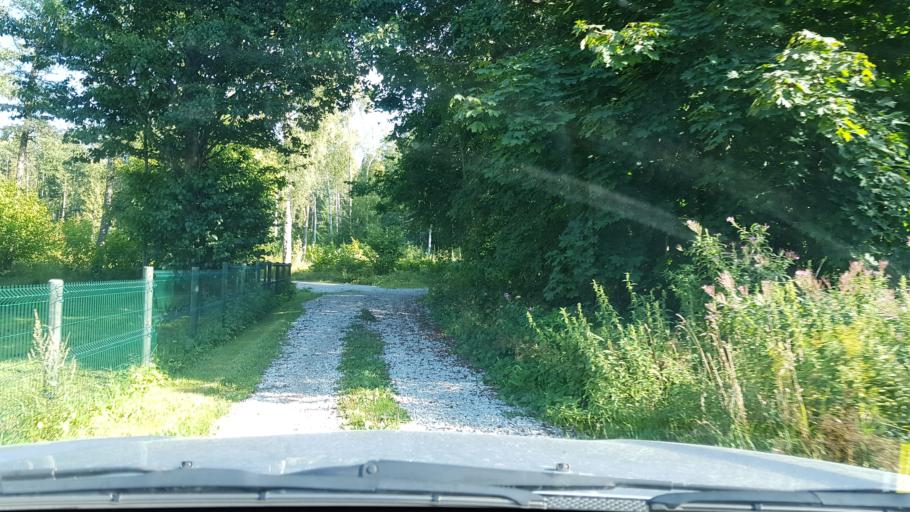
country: EE
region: Ida-Virumaa
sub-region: Narva-Joesuu linn
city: Narva-Joesuu
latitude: 59.4300
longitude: 27.9965
